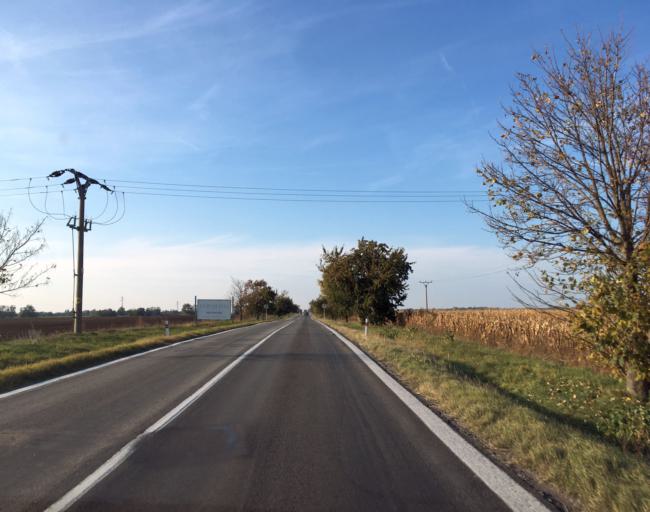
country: SK
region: Nitriansky
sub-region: Okres Nove Zamky
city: Nove Zamky
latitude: 48.0294
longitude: 18.1342
